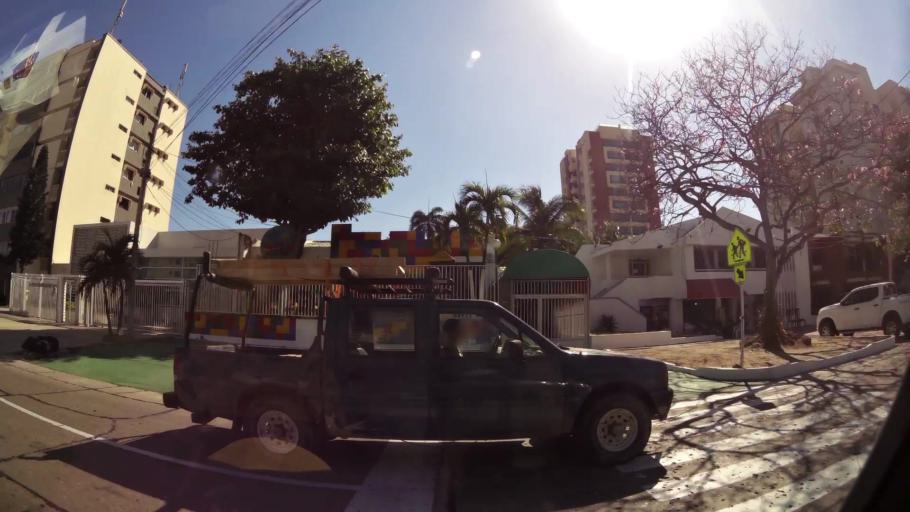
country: CO
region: Atlantico
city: Barranquilla
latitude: 11.0003
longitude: -74.8251
